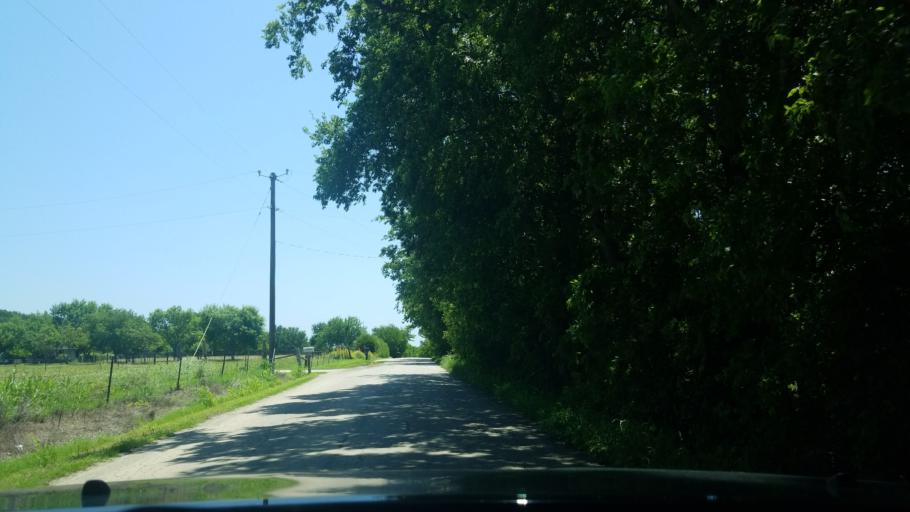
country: US
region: Texas
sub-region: Denton County
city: Sanger
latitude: 33.3504
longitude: -97.2061
